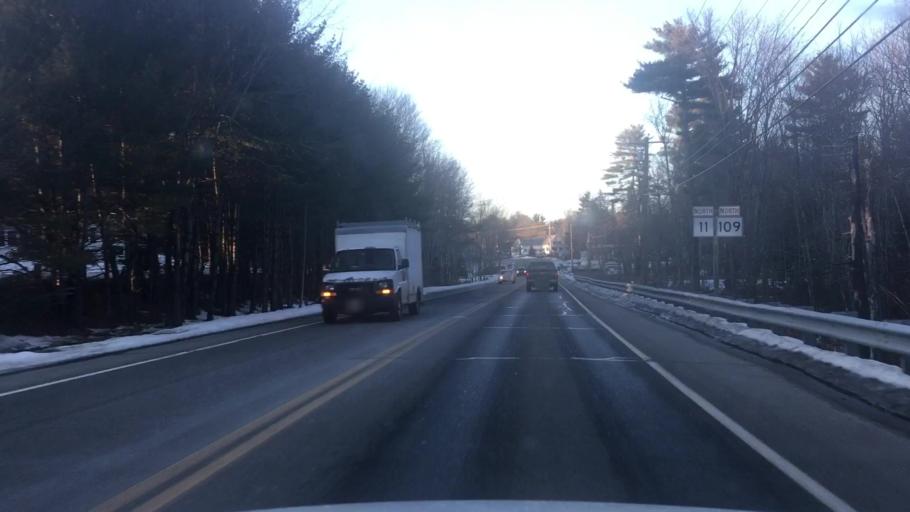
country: US
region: Maine
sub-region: York County
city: Springvale
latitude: 43.4733
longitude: -70.8102
